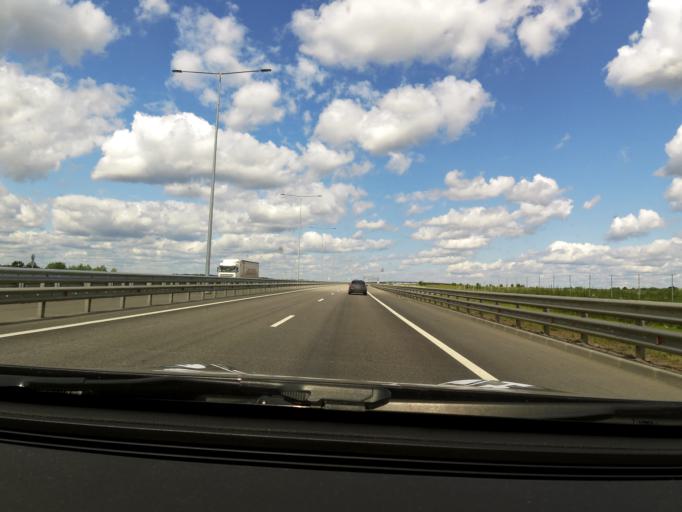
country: RU
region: Tverskaya
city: Vydropuzhsk
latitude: 57.2342
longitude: 34.9073
